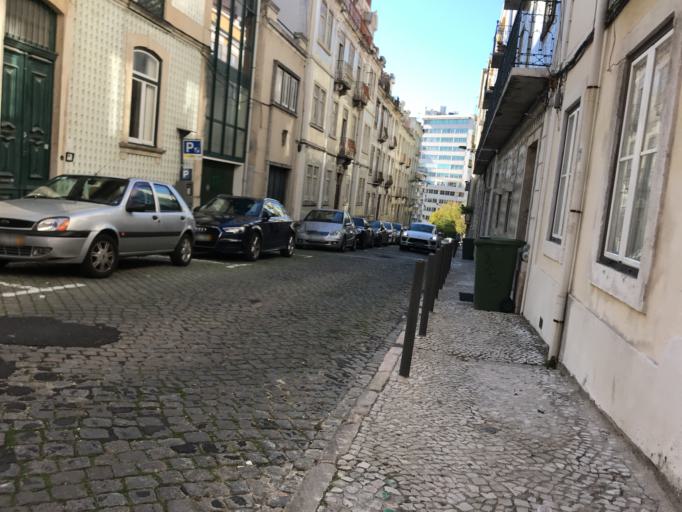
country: PT
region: Lisbon
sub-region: Lisbon
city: Lisbon
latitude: 38.7283
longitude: -9.1456
